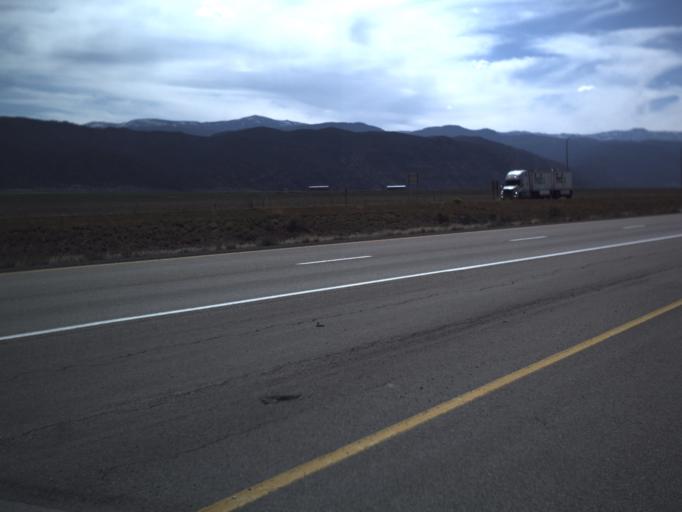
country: US
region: Utah
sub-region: Iron County
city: Parowan
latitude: 37.9799
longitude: -112.7387
